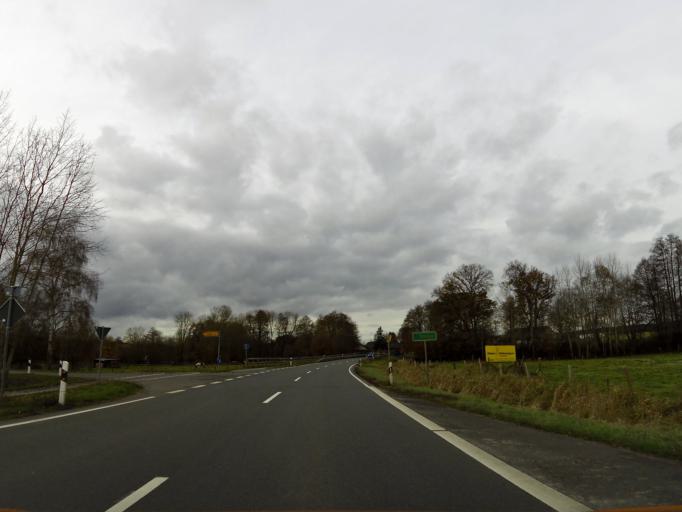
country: DE
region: Lower Saxony
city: Bergen an der Dumme
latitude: 52.8993
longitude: 10.9313
